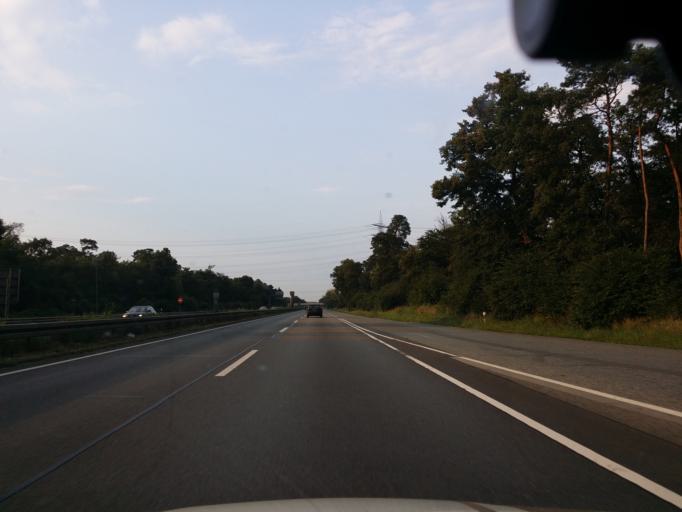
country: DE
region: Hesse
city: Pfungstadt
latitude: 49.8137
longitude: 8.5792
